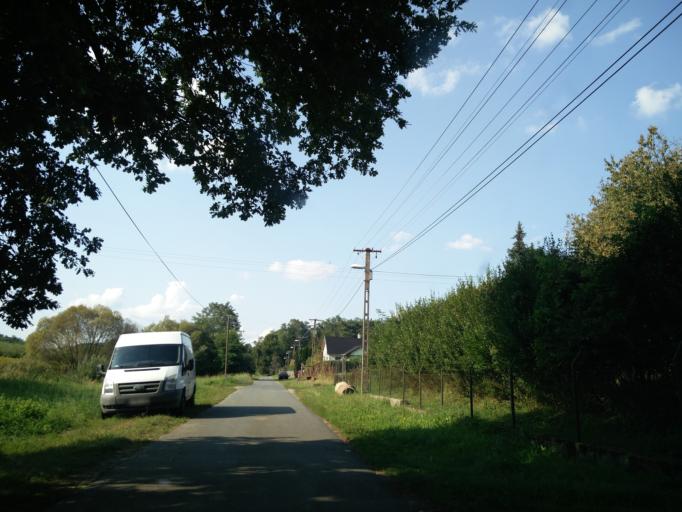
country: HU
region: Zala
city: Zalaegerszeg
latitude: 46.8741
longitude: 16.8489
